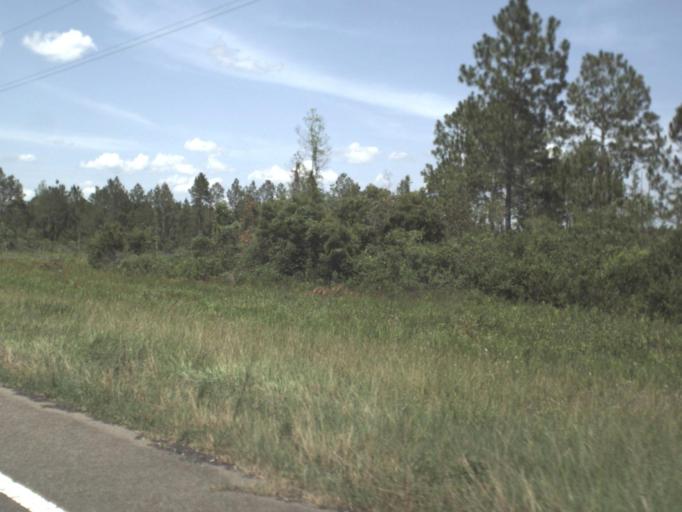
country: US
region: Florida
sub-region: Gilchrist County
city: Trenton
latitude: 29.6843
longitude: -82.7666
